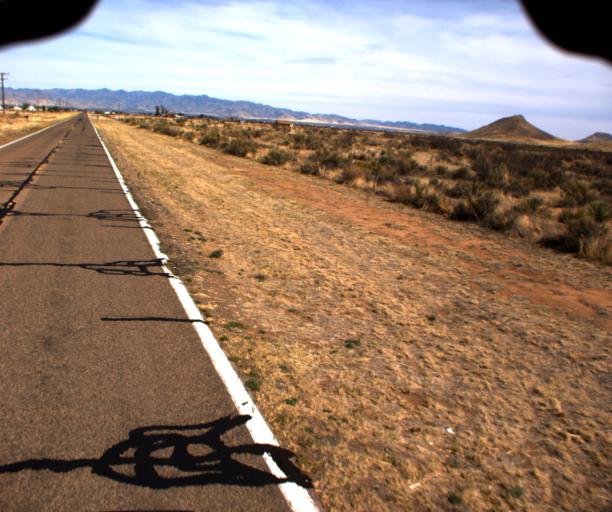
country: US
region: Arizona
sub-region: Cochise County
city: Willcox
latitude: 31.8837
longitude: -109.6852
